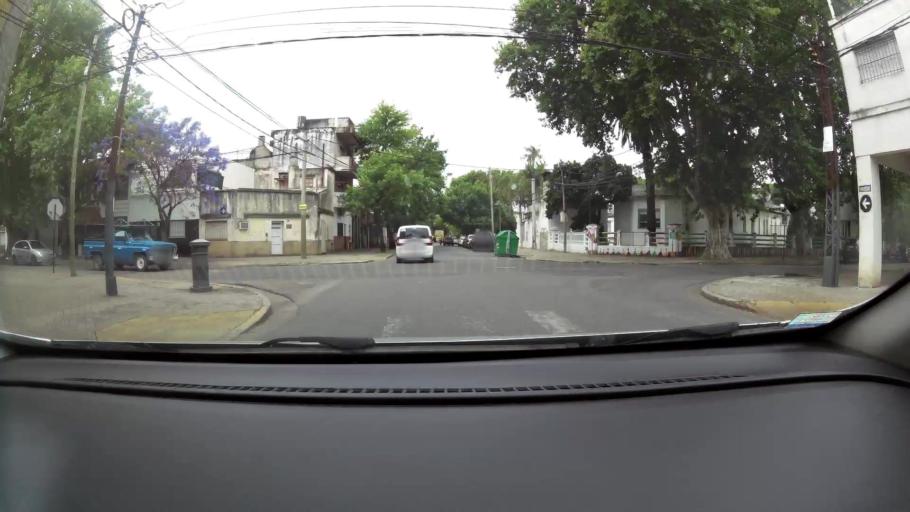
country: AR
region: Santa Fe
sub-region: Departamento de Rosario
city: Rosario
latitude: -32.9679
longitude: -60.6552
